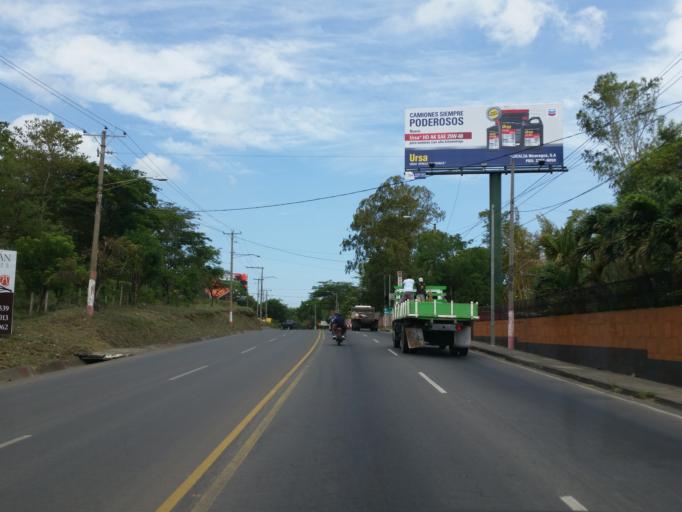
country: NI
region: Managua
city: Ciudad Sandino
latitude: 12.1069
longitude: -86.3240
